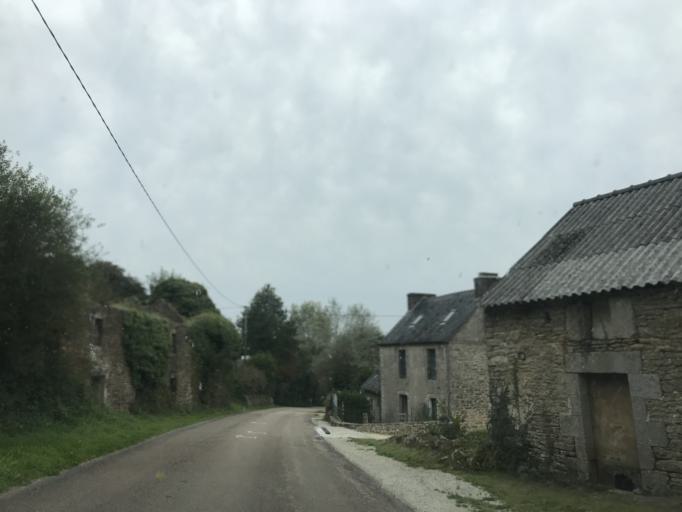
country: FR
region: Brittany
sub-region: Departement du Finistere
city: Plouneour-Menez
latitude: 48.3867
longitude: -3.8693
